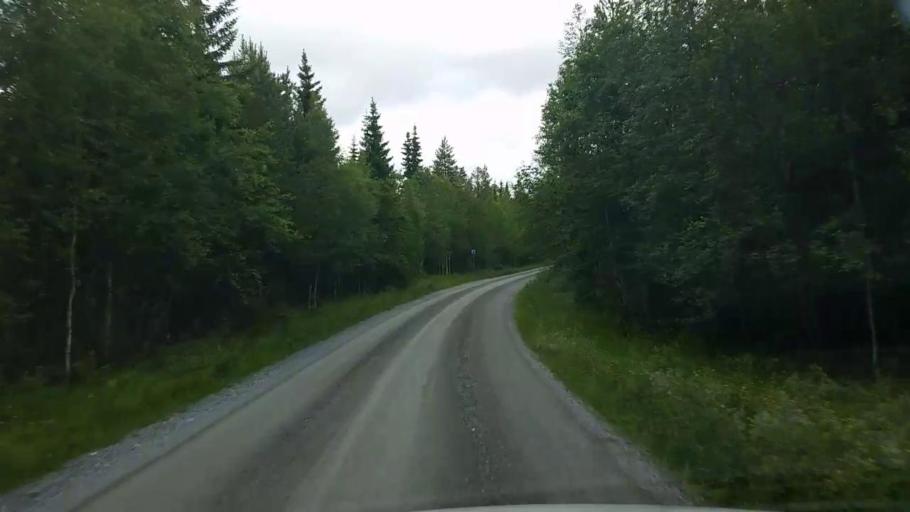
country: NO
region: Hedmark
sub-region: Engerdal
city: Engerdal
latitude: 62.4102
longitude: 12.6722
